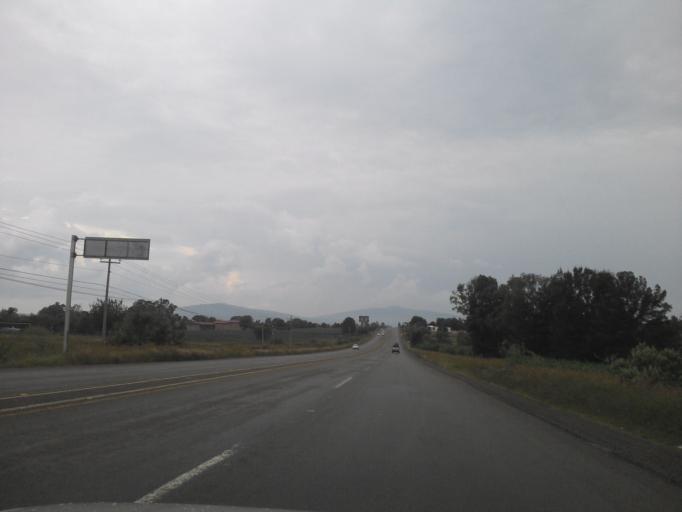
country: MX
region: Jalisco
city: Arandas
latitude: 20.7234
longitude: -102.4593
